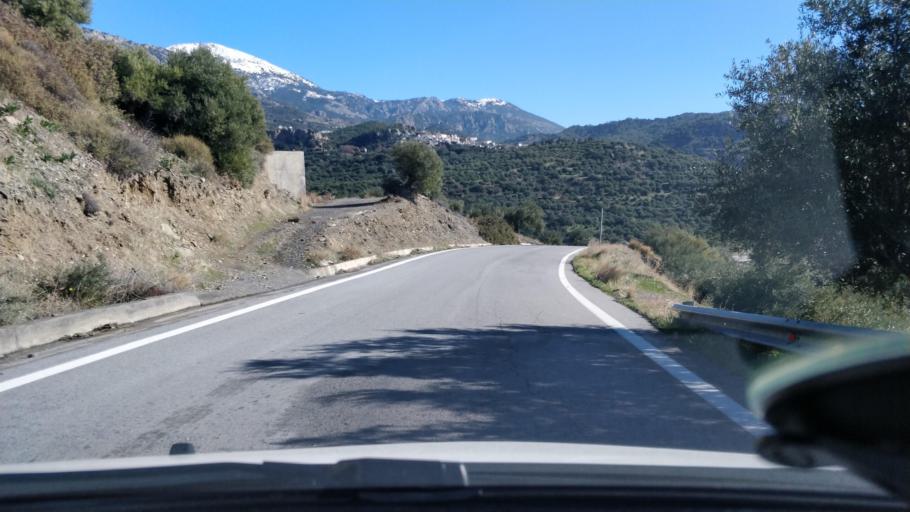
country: GR
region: Crete
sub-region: Nomos Irakleiou
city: Kastelli
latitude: 35.0316
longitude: 25.4463
